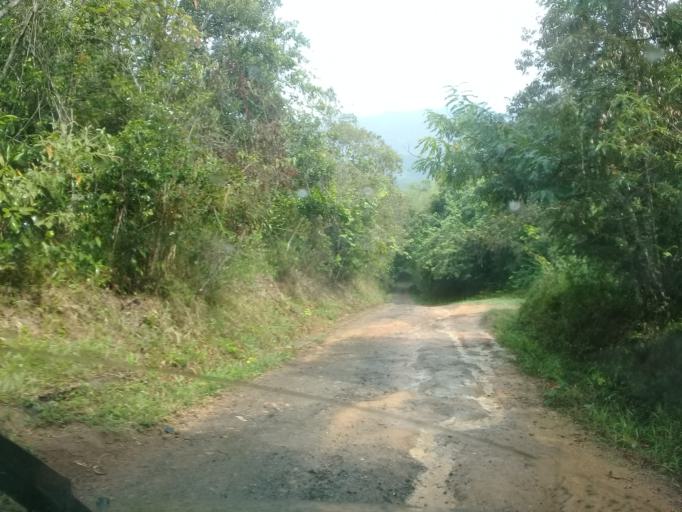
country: CO
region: Cundinamarca
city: Guaduas
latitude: 5.1022
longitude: -74.6079
